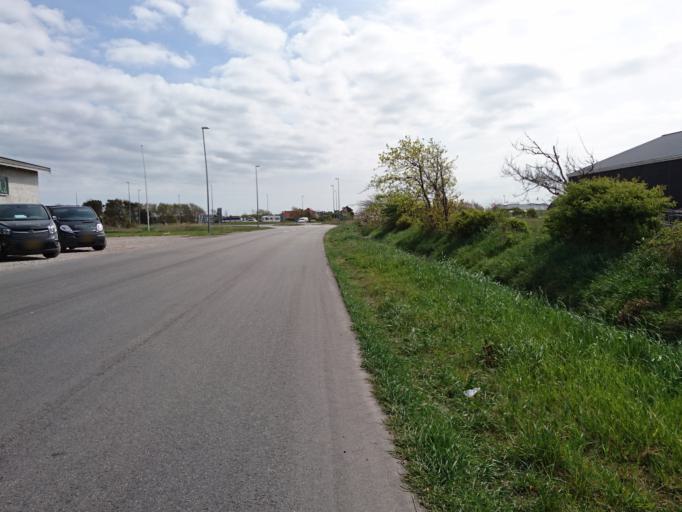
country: DK
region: North Denmark
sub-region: Frederikshavn Kommune
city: Skagen
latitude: 57.7317
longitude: 10.5689
